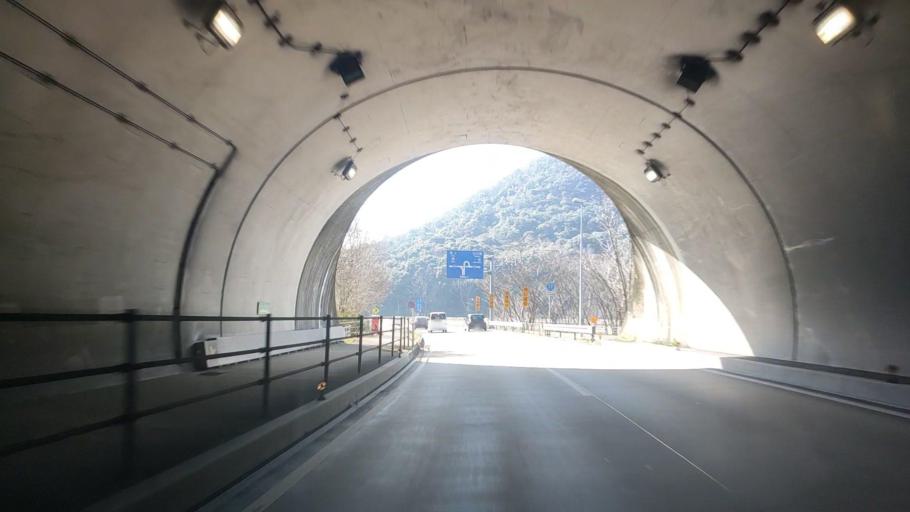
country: JP
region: Gifu
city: Gifu-shi
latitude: 35.4319
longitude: 136.7962
